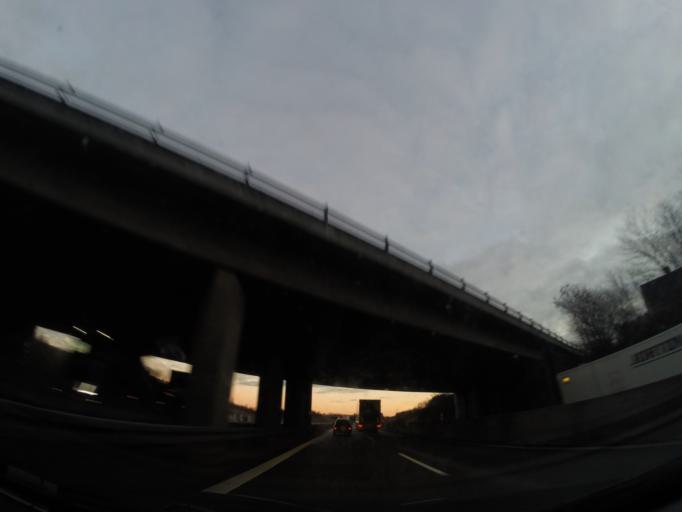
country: DK
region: Zealand
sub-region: Slagelse Kommune
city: Slagelse
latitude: 55.4177
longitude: 11.4138
